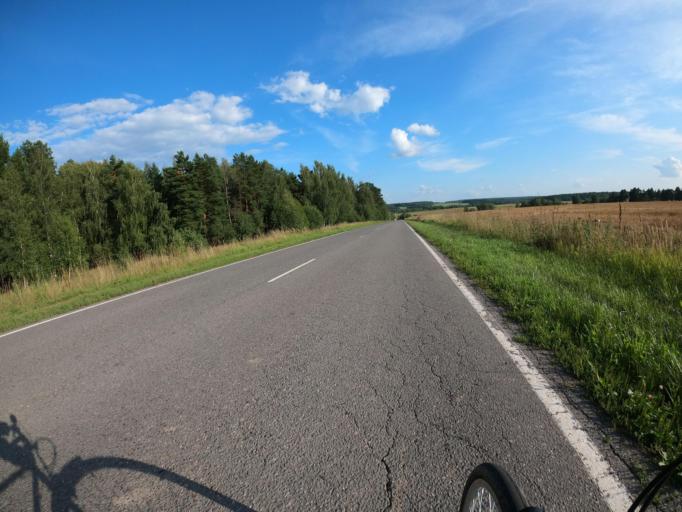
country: RU
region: Moskovskaya
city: Meshcherino
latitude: 55.1519
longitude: 38.4330
